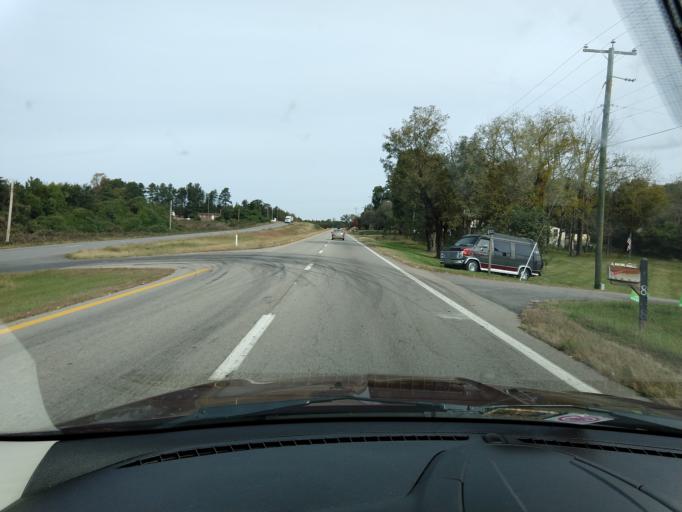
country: US
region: Virginia
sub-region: Pittsylvania County
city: Chatham
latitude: 36.8777
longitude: -79.4087
